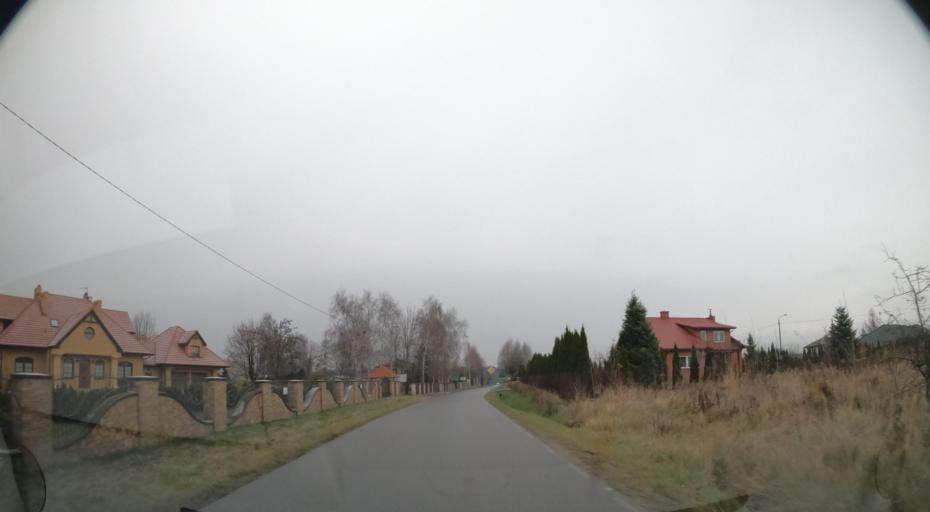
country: PL
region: Masovian Voivodeship
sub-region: Radom
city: Radom
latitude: 51.4189
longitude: 21.2243
